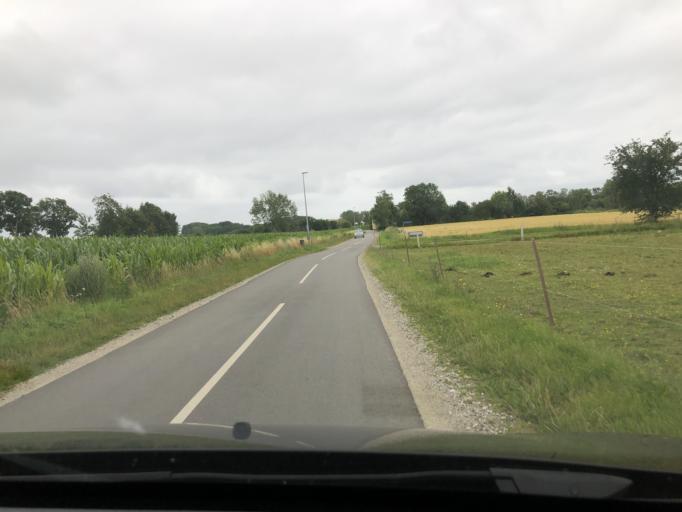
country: DK
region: South Denmark
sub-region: AEro Kommune
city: Marstal
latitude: 54.8547
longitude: 10.4788
